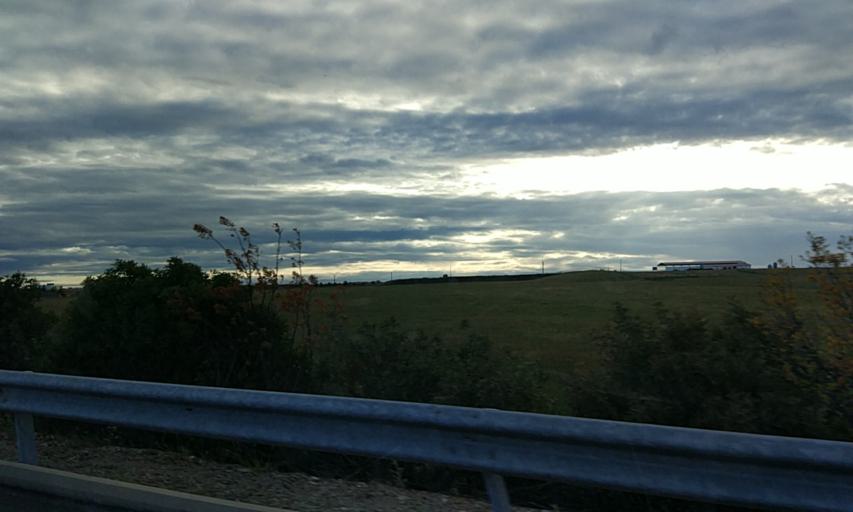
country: ES
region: Extremadura
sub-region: Provincia de Caceres
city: Casar de Caceres
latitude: 39.5225
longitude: -6.4185
